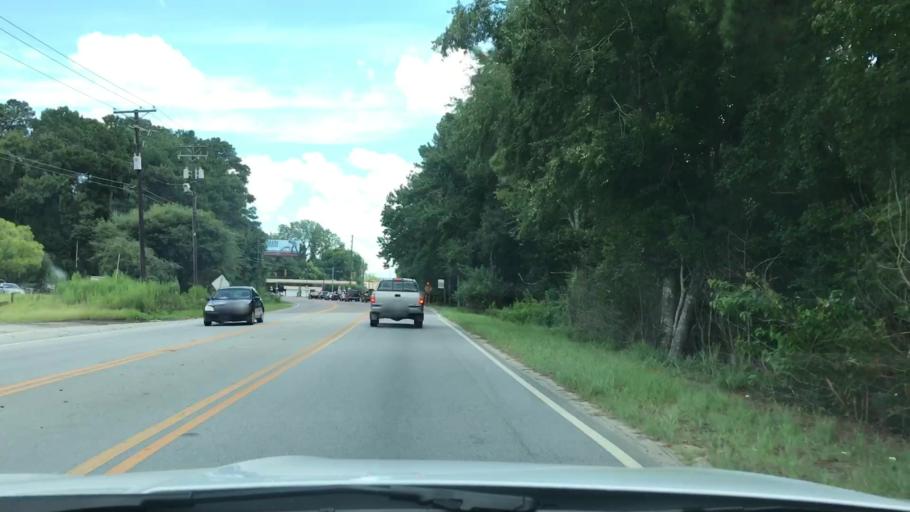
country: US
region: South Carolina
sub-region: Dorchester County
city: Summerville
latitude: 33.0346
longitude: -80.2007
